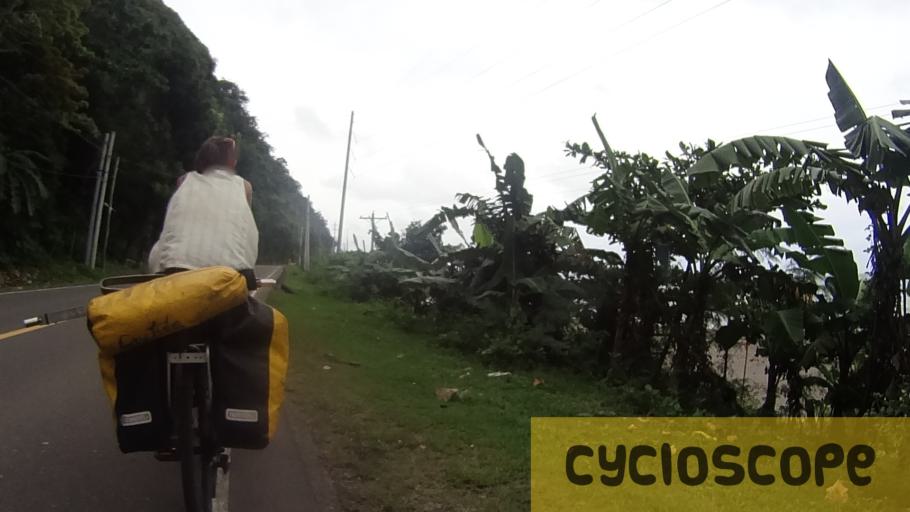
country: PH
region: Western Visayas
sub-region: Province of Aklan
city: Gibong
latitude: 11.8662
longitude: 122.0359
